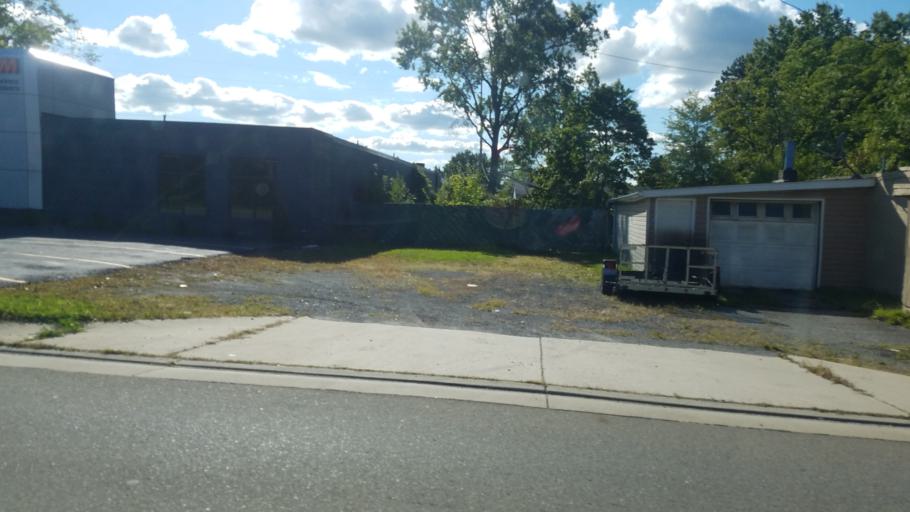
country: US
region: Ohio
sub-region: Mahoning County
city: Austintown
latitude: 41.1034
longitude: -80.7643
